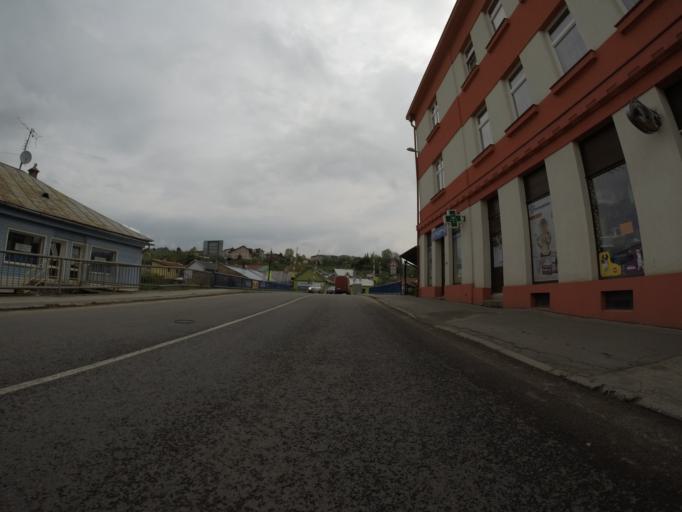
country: SK
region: Banskobystricky
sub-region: Okres Banska Bystrica
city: Brezno
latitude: 48.8060
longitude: 19.6460
